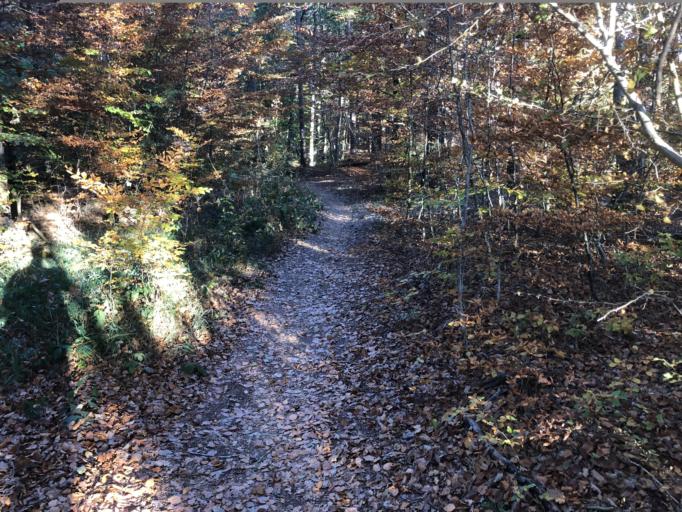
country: DE
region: Baden-Wuerttemberg
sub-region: Regierungsbezirk Stuttgart
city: Hildrizhausen
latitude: 48.5742
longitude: 8.9759
